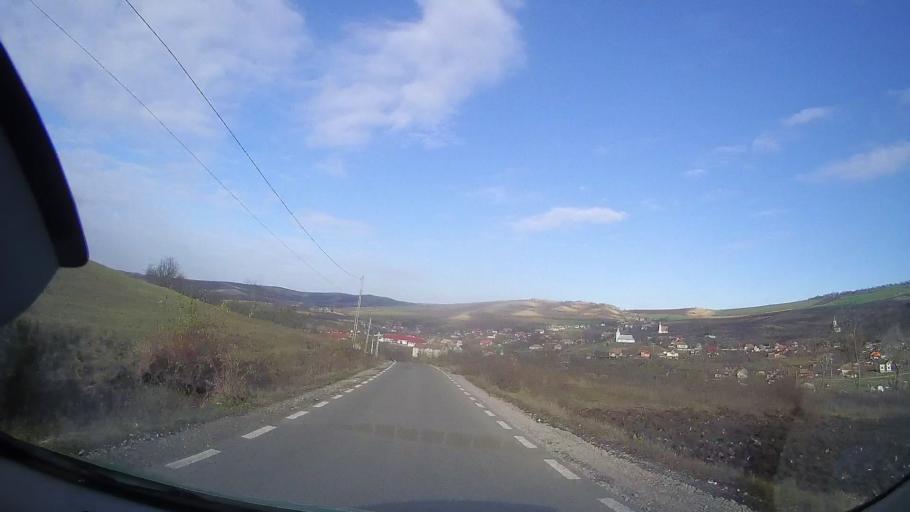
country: RO
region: Mures
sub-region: Comuna Sanger
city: Sanger
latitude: 46.5535
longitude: 24.1426
